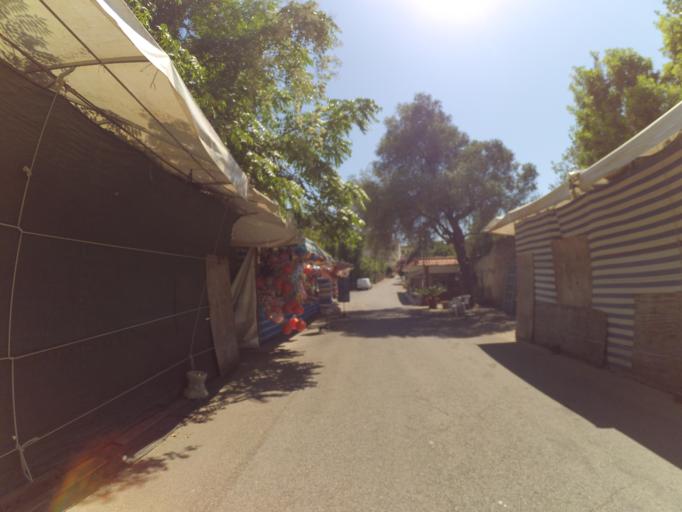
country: IT
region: Latium
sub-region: Provincia di Latina
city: Gaeta
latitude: 41.2064
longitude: 13.5715
